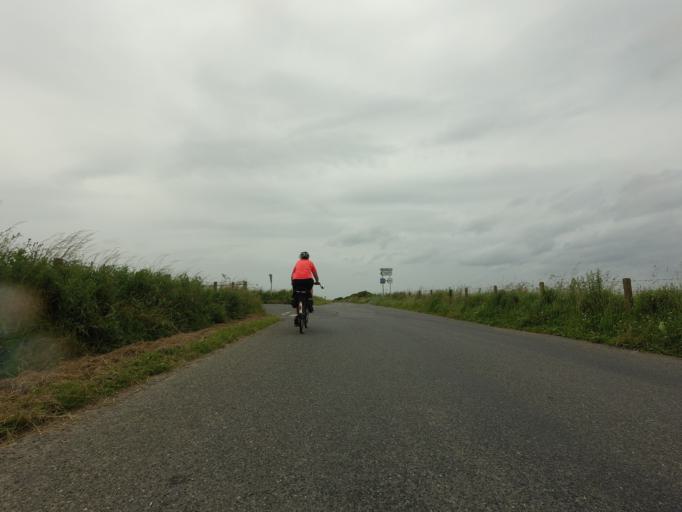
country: GB
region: Scotland
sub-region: Moray
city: Cullen
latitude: 57.6637
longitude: -2.7598
